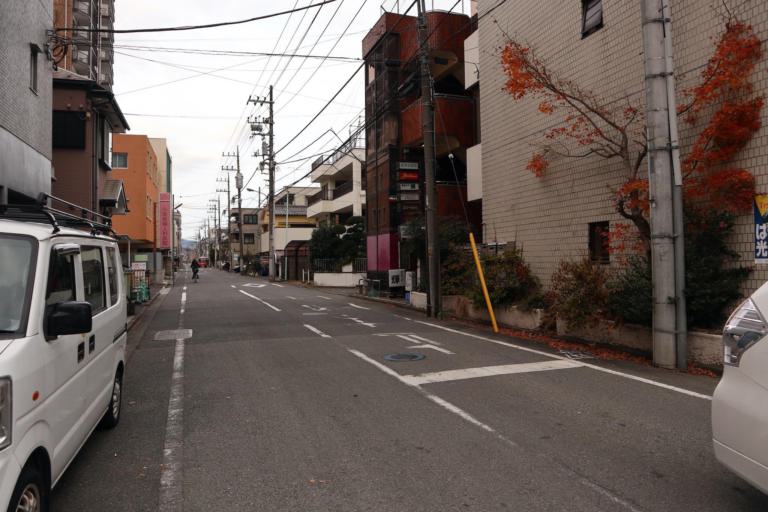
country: JP
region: Tokyo
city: Hachioji
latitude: 35.6611
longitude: 139.3288
